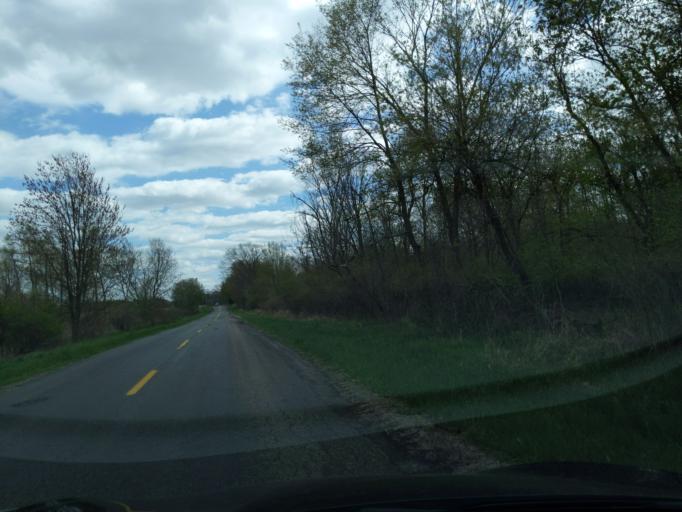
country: US
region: Michigan
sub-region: Eaton County
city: Eaton Rapids
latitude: 42.5175
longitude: -84.5421
